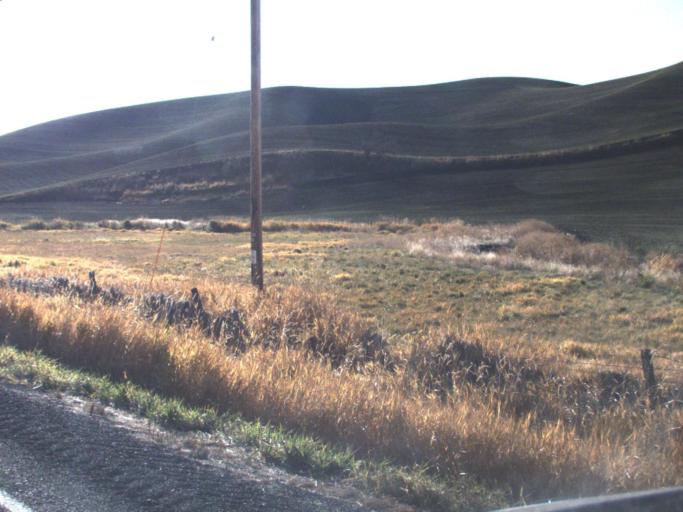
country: US
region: Washington
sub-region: Whitman County
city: Colfax
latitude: 46.7674
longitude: -117.3923
